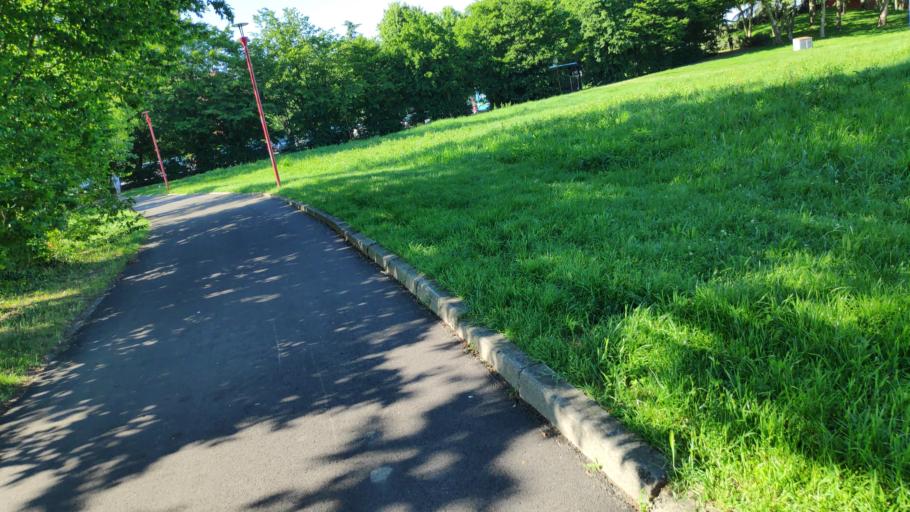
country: IT
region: Lombardy
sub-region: Citta metropolitana di Milano
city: Basiglio
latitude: 45.3570
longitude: 9.1550
